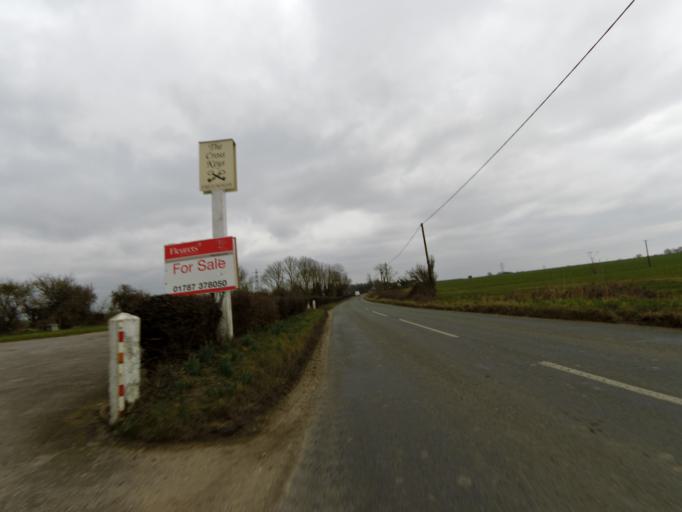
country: GB
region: England
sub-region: Suffolk
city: Ipswich
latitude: 52.1276
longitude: 1.1449
